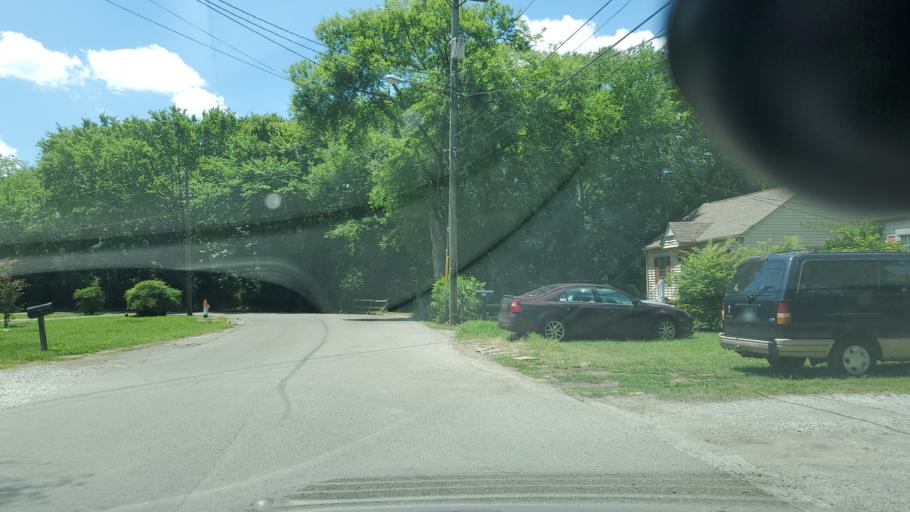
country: US
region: Tennessee
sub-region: Davidson County
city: Nashville
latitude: 36.1900
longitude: -86.7524
